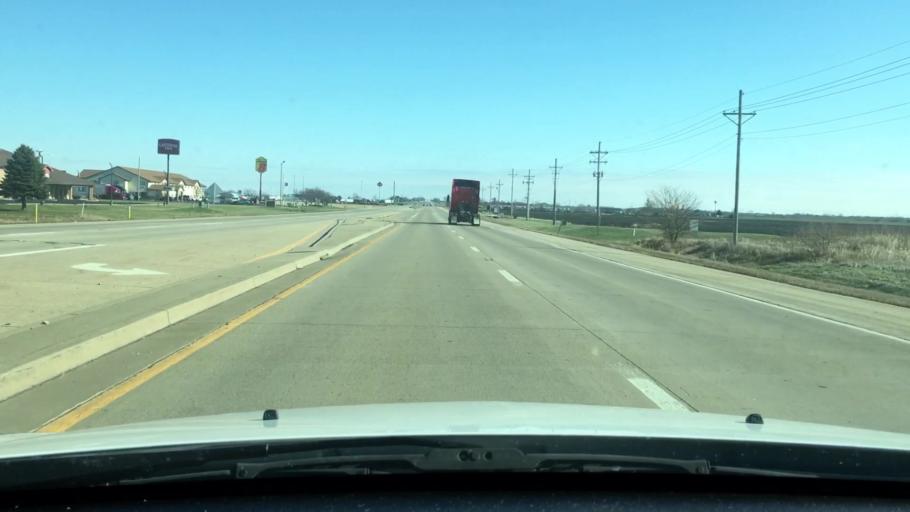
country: US
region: Illinois
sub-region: Ogle County
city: Rochelle
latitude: 41.9343
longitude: -89.0468
